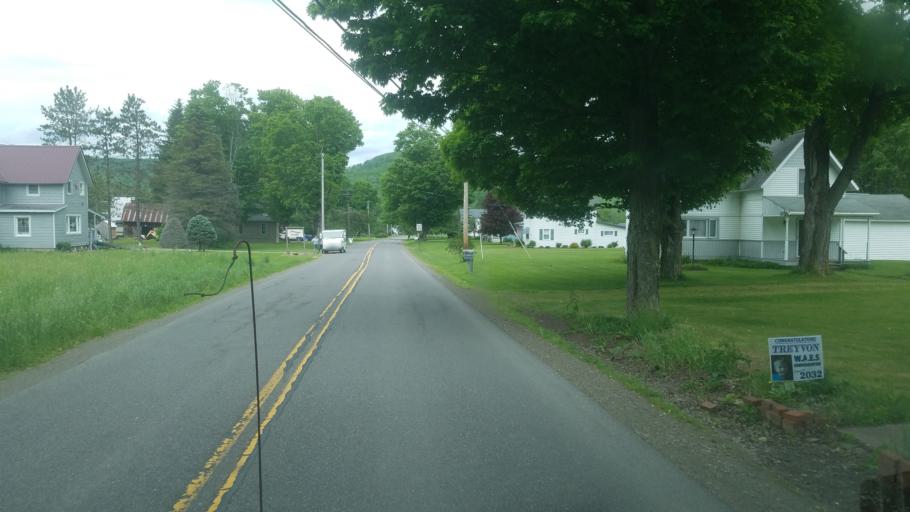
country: US
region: Pennsylvania
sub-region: Tioga County
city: Westfield
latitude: 41.9044
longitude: -77.6050
